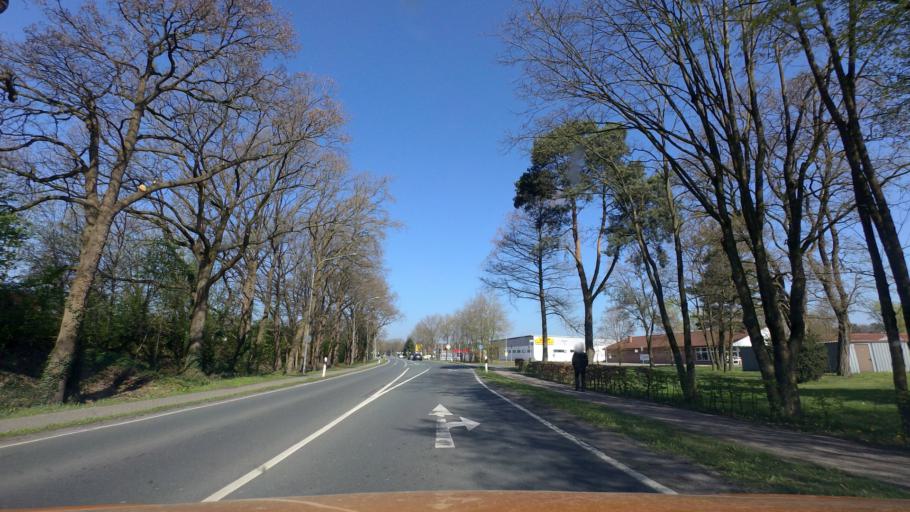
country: DE
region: Lower Saxony
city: Wardenburg
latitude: 53.0553
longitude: 8.2022
